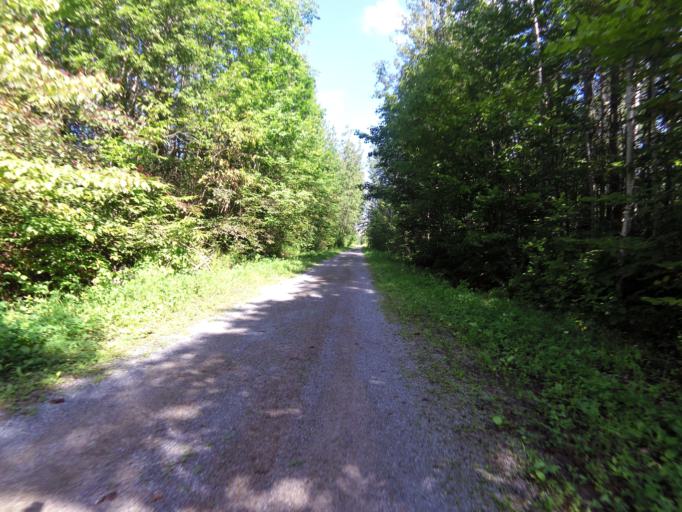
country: CA
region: Ontario
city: Ottawa
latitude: 45.2002
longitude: -75.6235
